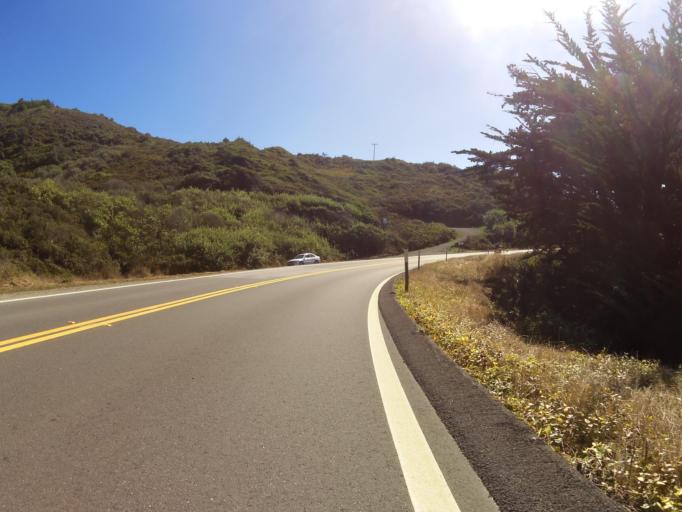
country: US
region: California
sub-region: Mendocino County
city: Fort Bragg
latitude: 39.6082
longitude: -123.7835
